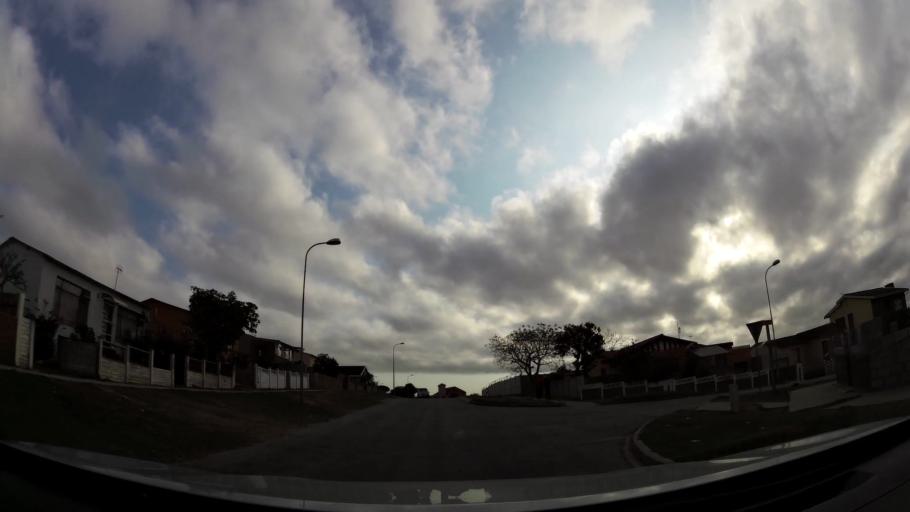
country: ZA
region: Eastern Cape
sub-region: Nelson Mandela Bay Metropolitan Municipality
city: Port Elizabeth
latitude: -33.9131
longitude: 25.5502
